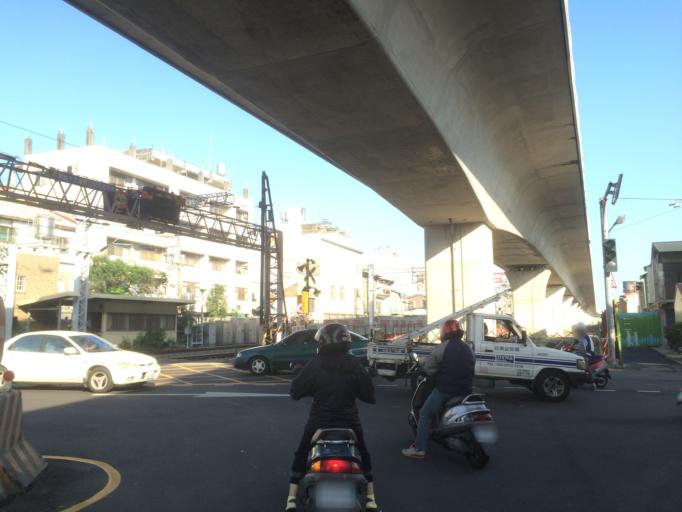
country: TW
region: Taiwan
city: Fengyuan
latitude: 24.2154
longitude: 120.7062
